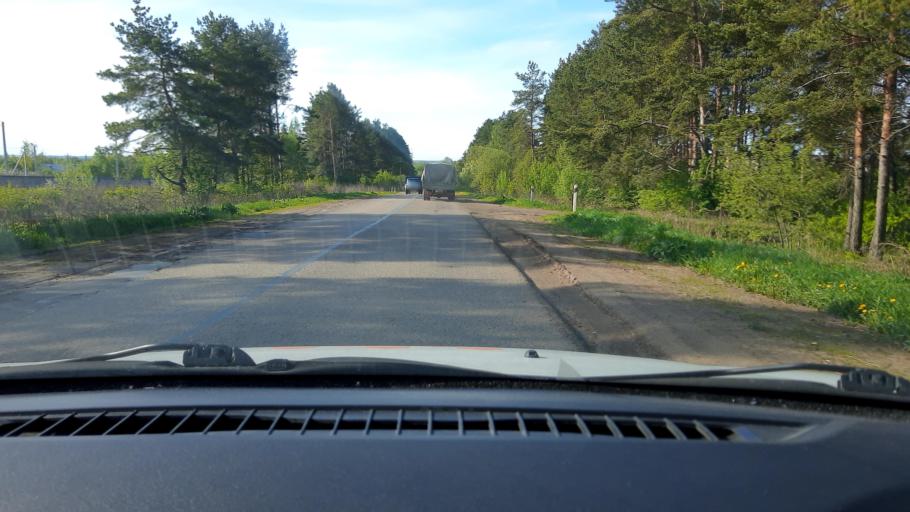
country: RU
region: Nizjnij Novgorod
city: Burevestnik
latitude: 56.1508
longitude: 43.7772
